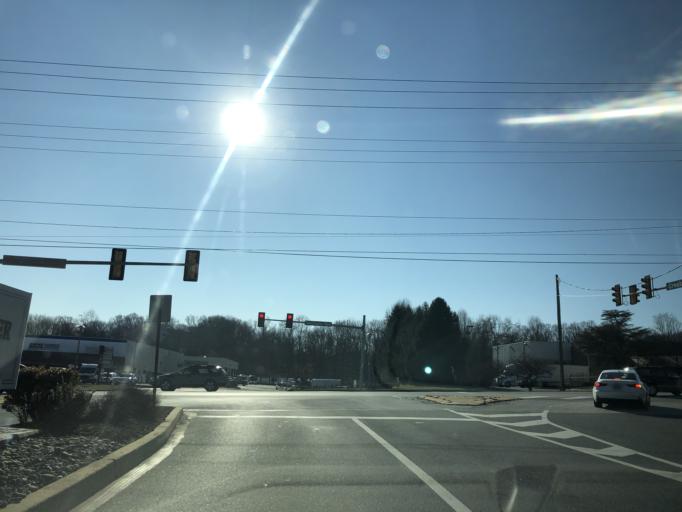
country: US
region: Pennsylvania
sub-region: Delaware County
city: Boothwyn
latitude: 39.8530
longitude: -75.4608
